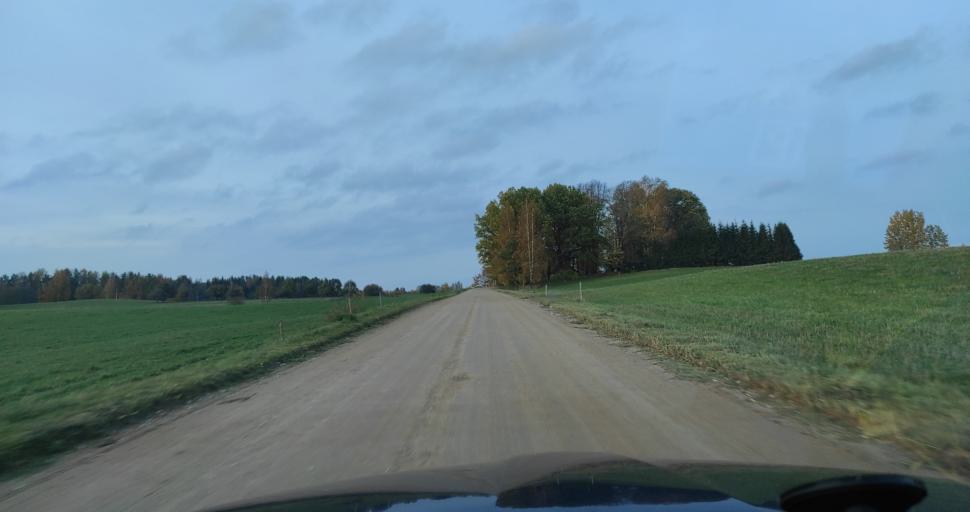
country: LV
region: Aizpute
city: Aizpute
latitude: 56.6541
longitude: 21.7948
